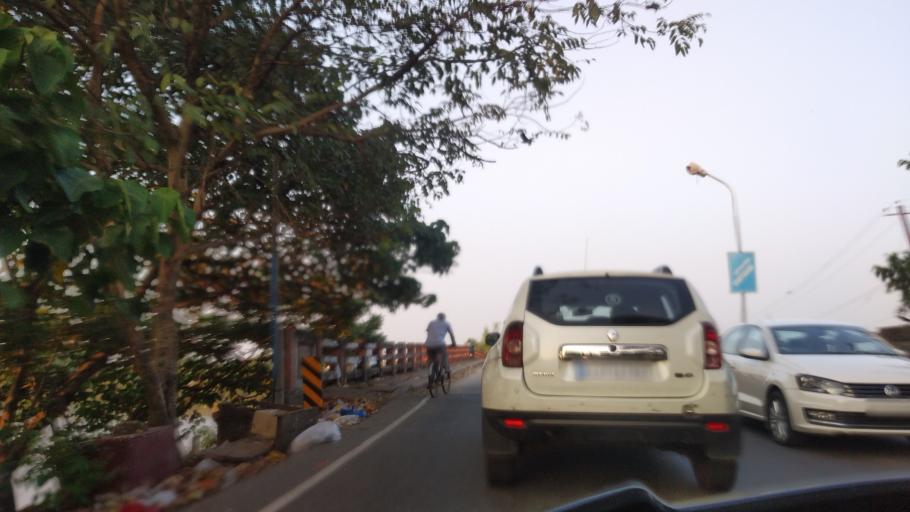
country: IN
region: Kerala
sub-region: Ernakulam
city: Elur
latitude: 10.0247
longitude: 76.2742
